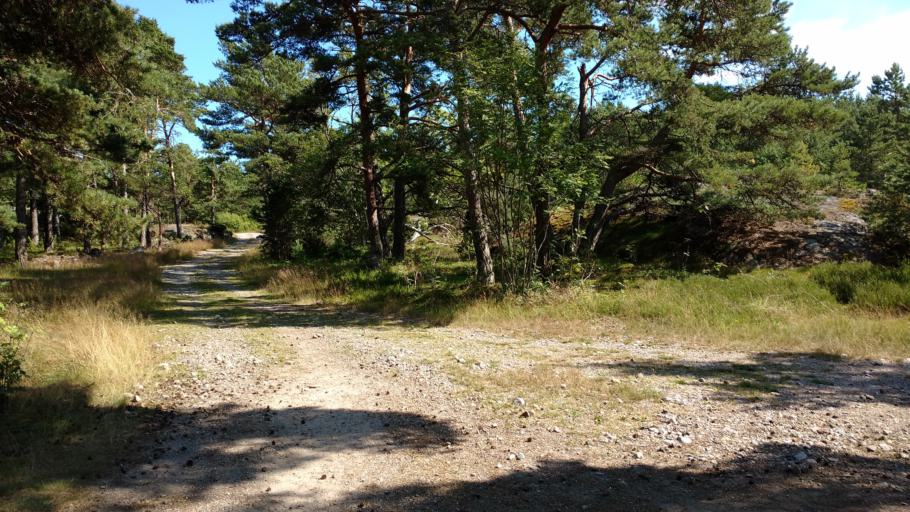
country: FI
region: Varsinais-Suomi
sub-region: Aboland-Turunmaa
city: Dragsfjaerd
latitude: 59.8081
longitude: 22.3272
